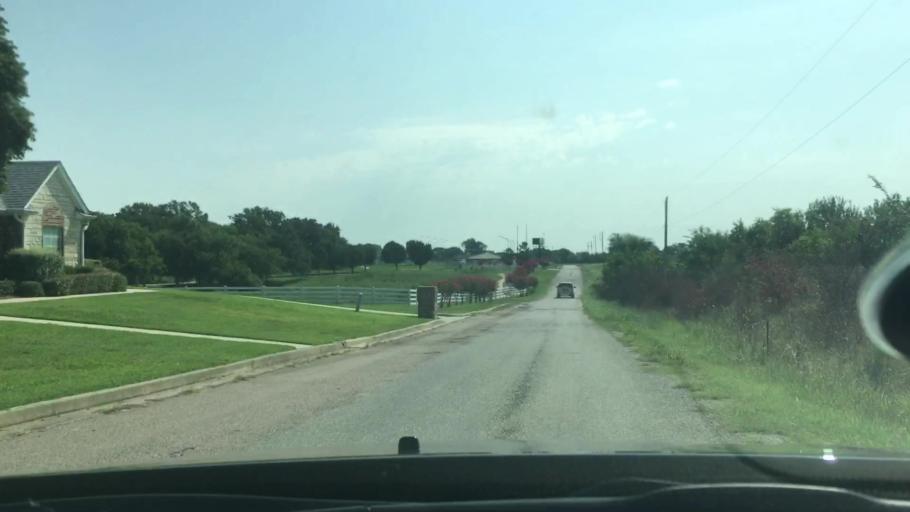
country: US
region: Oklahoma
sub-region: Bryan County
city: Durant
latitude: 34.0557
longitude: -96.3604
